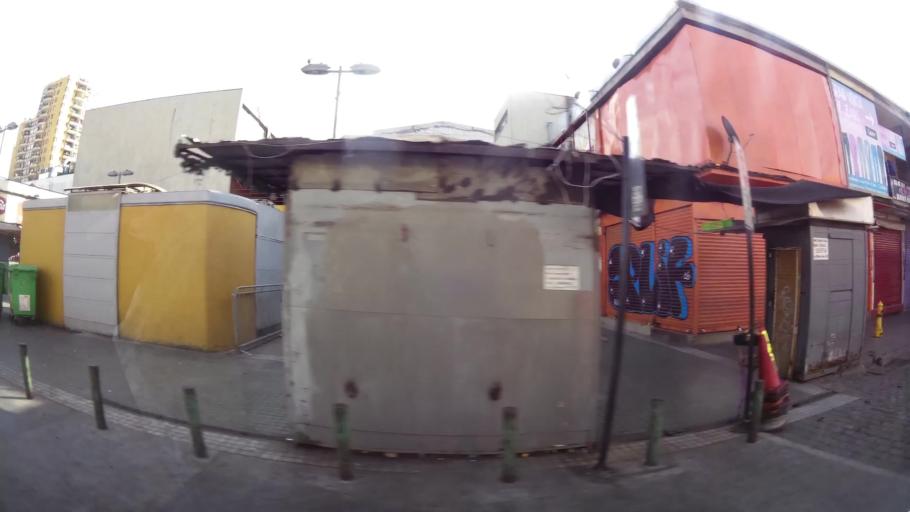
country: CL
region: Santiago Metropolitan
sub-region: Provincia de Santiago
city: Santiago
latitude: -33.4519
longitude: -70.6764
